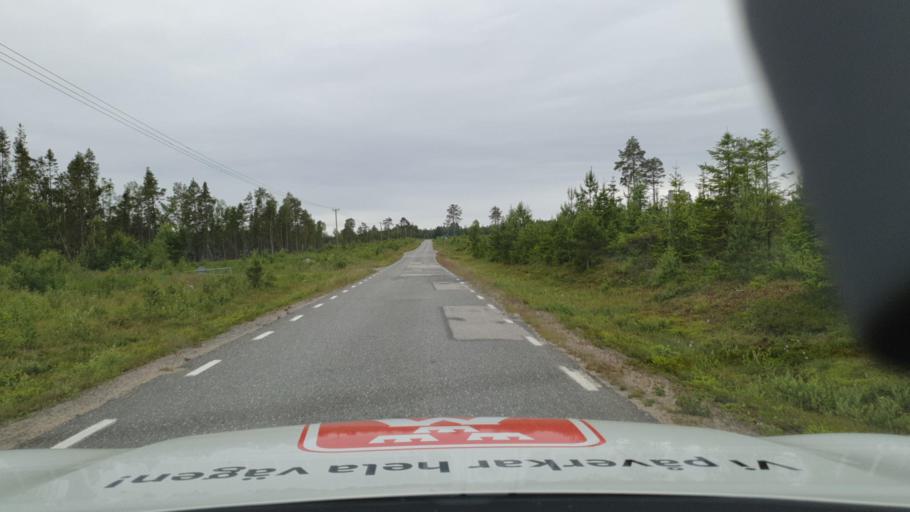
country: SE
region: Vaesterbotten
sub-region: Nordmalings Kommun
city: Nordmaling
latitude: 63.4513
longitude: 19.4678
